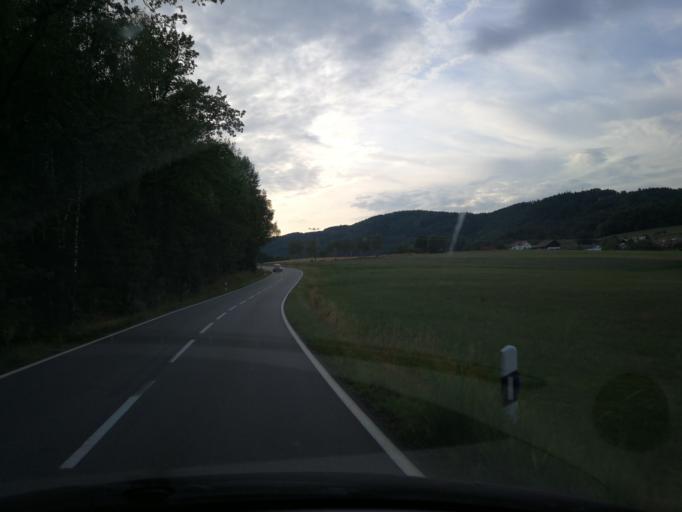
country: DE
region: Bavaria
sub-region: Lower Bavaria
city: Haibach
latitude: 49.0317
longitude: 12.7052
